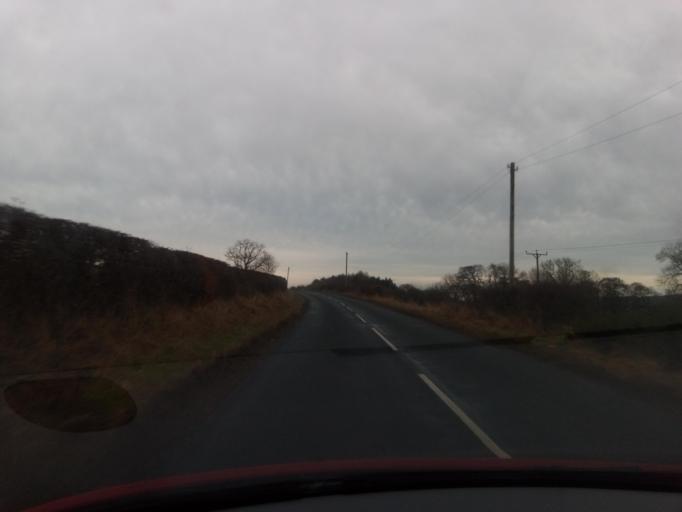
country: GB
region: England
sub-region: Northumberland
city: Whittingham
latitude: 55.4600
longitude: -1.8125
